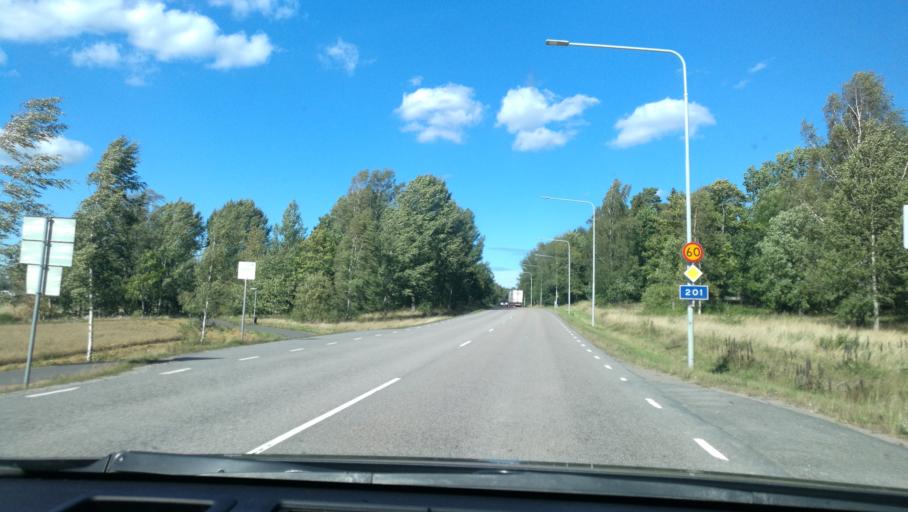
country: SE
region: Vaestra Goetaland
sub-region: Mariestads Kommun
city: Mariestad
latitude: 58.6862
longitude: 13.8444
